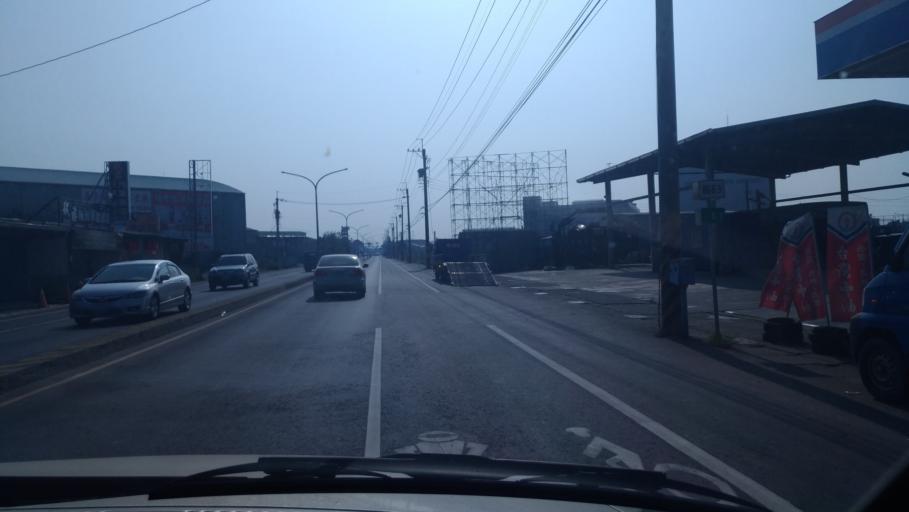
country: TW
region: Taiwan
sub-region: Chiayi
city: Jiayi Shi
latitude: 23.5226
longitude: 120.4235
